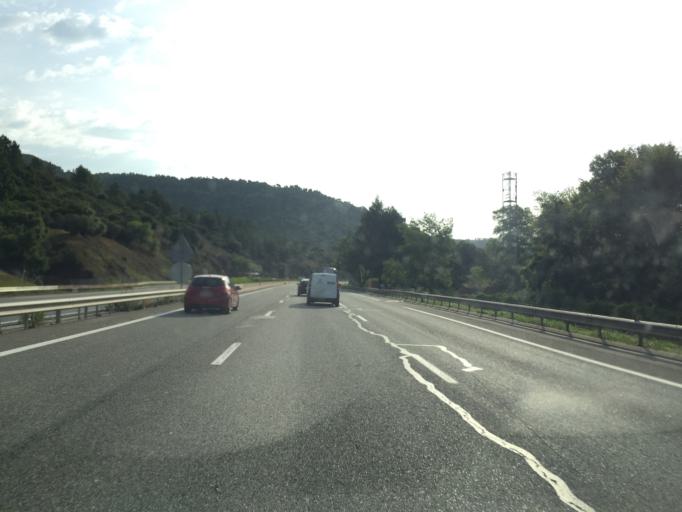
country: FR
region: Provence-Alpes-Cote d'Azur
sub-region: Departement du Var
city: Tanneron
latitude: 43.5388
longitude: 6.8386
